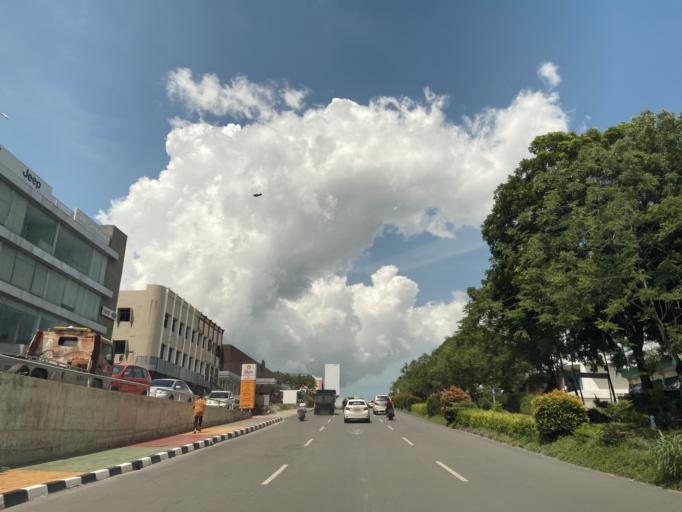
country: SG
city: Singapore
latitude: 1.1367
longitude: 104.0167
